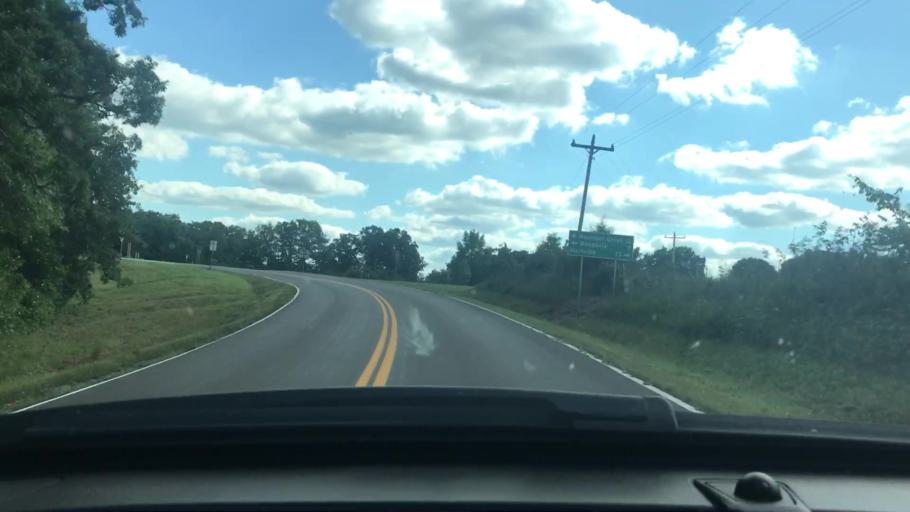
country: US
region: Missouri
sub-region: Wright County
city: Mountain Grove
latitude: 37.3017
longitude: -92.3130
